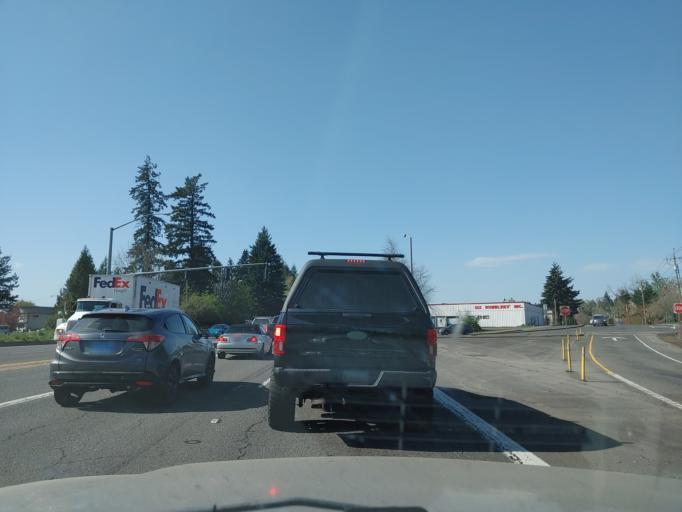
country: US
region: Oregon
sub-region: Clackamas County
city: Milwaukie
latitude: 45.4389
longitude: -122.6243
